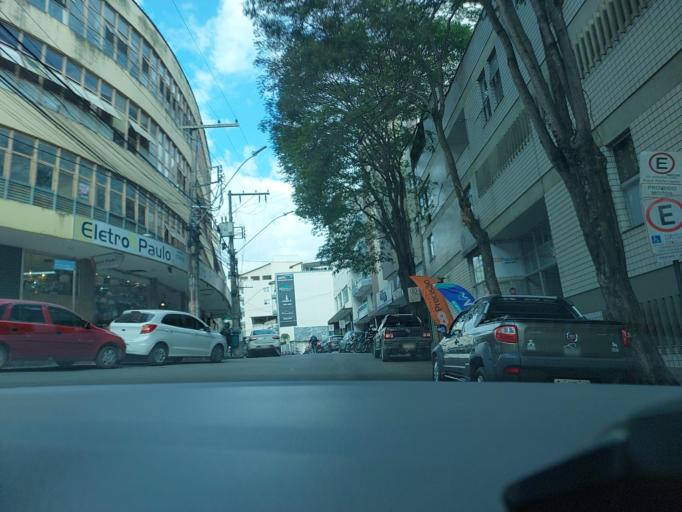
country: BR
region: Minas Gerais
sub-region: Vicosa
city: Vicosa
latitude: -20.7526
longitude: -42.8802
